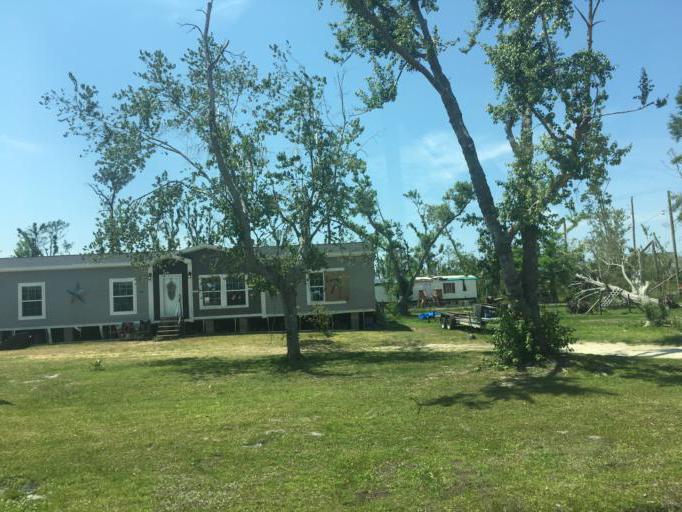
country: US
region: Florida
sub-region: Bay County
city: Hiland Park
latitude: 30.2105
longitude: -85.6327
